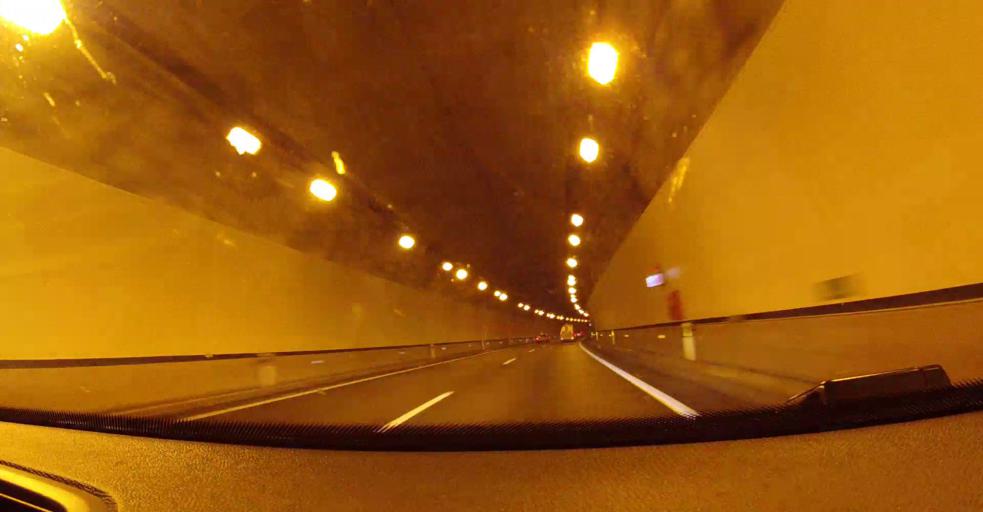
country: ES
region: Basque Country
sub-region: Provincia de Guipuzcoa
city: Bergara
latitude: 43.1174
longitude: -2.4290
